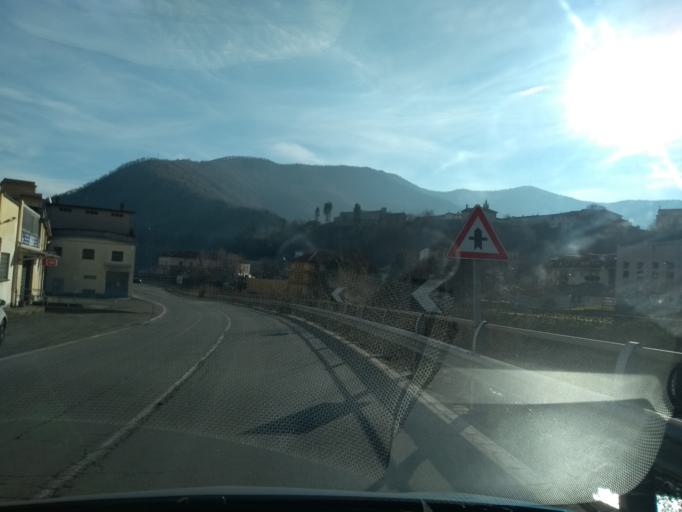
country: IT
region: Piedmont
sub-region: Provincia di Torino
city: Lanzo Torinese
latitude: 45.2757
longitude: 7.4795
